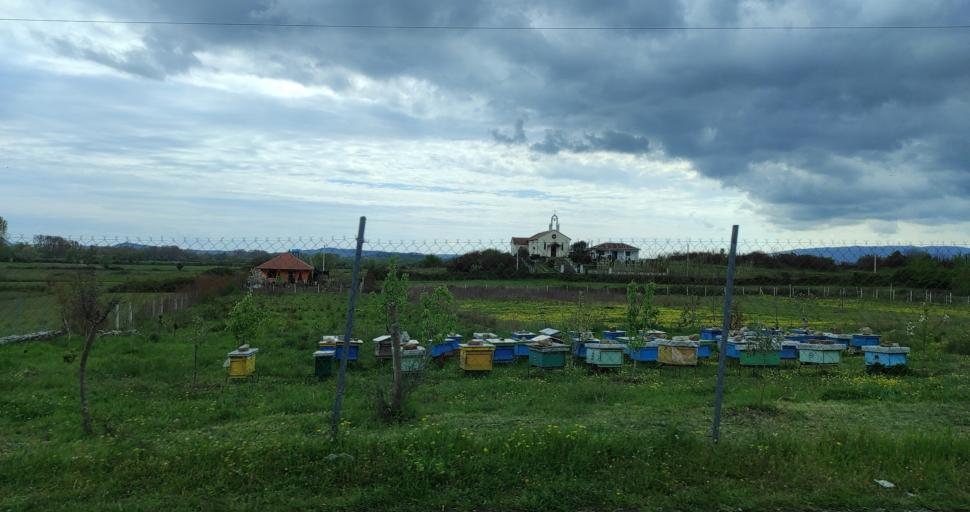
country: AL
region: Shkoder
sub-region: Rrethi i Shkodres
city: Dajc
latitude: 42.0158
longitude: 19.3996
